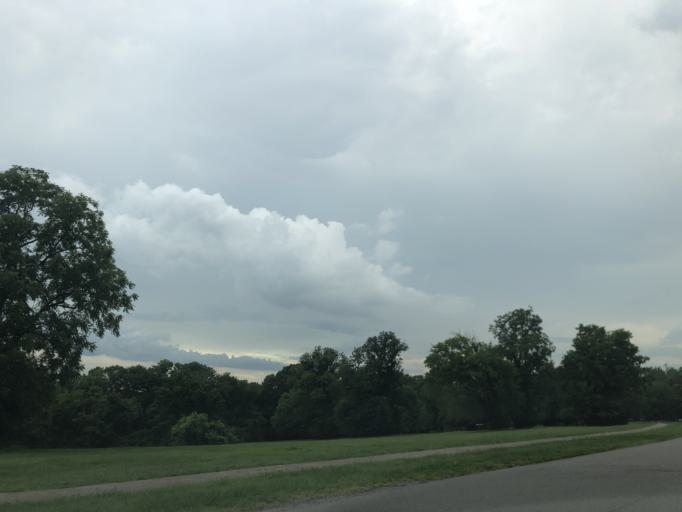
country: US
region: Tennessee
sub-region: Davidson County
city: Lakewood
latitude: 36.1778
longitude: -86.6838
